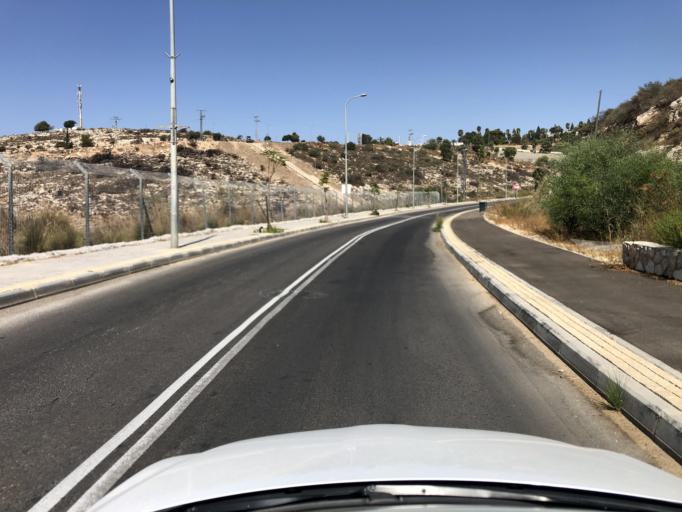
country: PS
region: West Bank
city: An Nabi Ilyas
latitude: 32.1684
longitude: 35.0048
